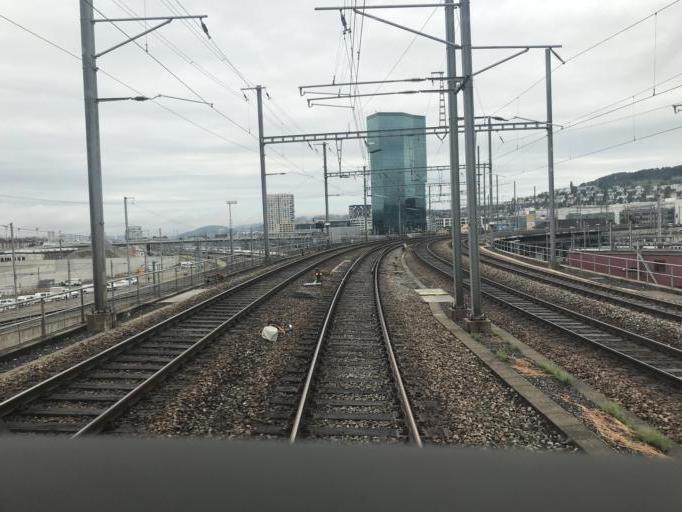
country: CH
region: Zurich
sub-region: Bezirk Zuerich
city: Aussersihl
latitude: 47.3821
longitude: 8.5219
